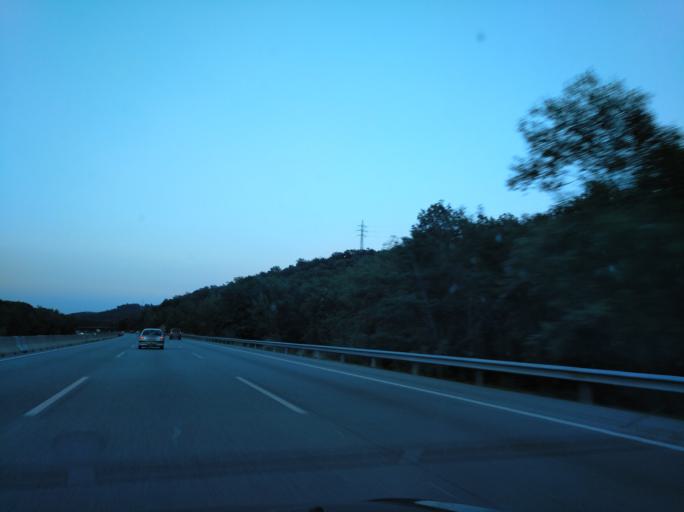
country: ES
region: Catalonia
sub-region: Provincia de Girona
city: Breda
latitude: 41.7141
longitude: 2.5520
